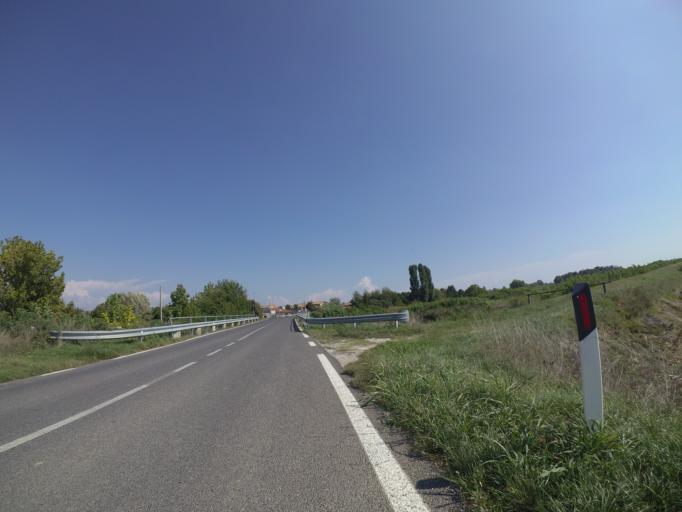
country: IT
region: Friuli Venezia Giulia
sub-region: Provincia di Udine
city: Muzzana del Turgnano
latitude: 45.8127
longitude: 13.1575
